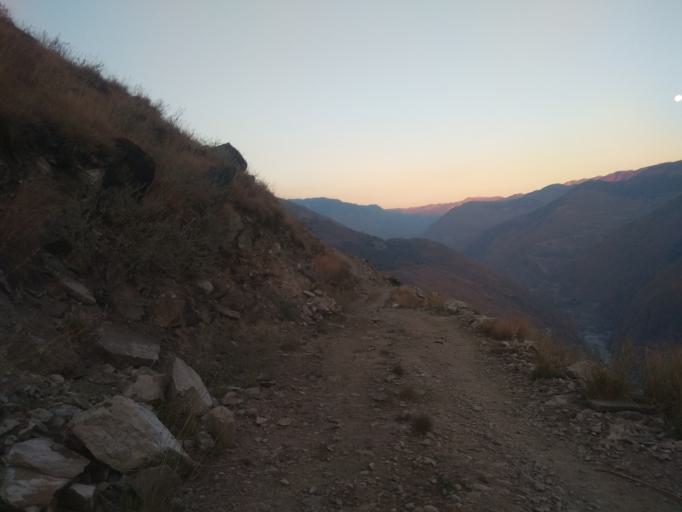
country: NP
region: Mid Western
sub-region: Bheri Zone
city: Dailekh
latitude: 29.2655
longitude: 81.6909
